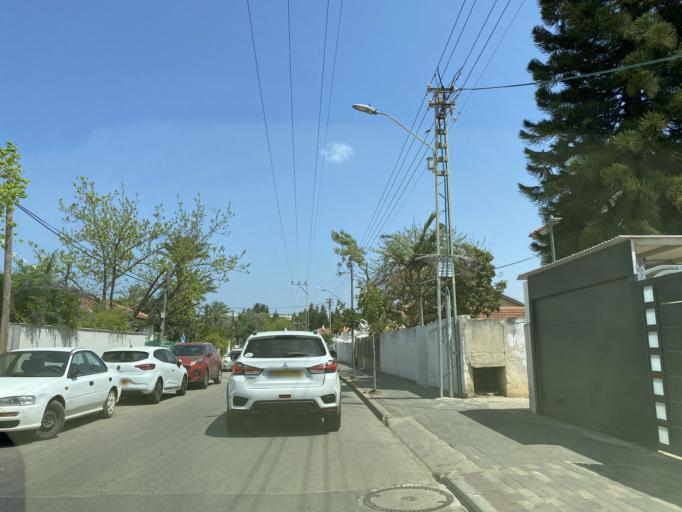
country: IL
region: Tel Aviv
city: Ramat HaSharon
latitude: 32.1544
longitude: 34.8365
